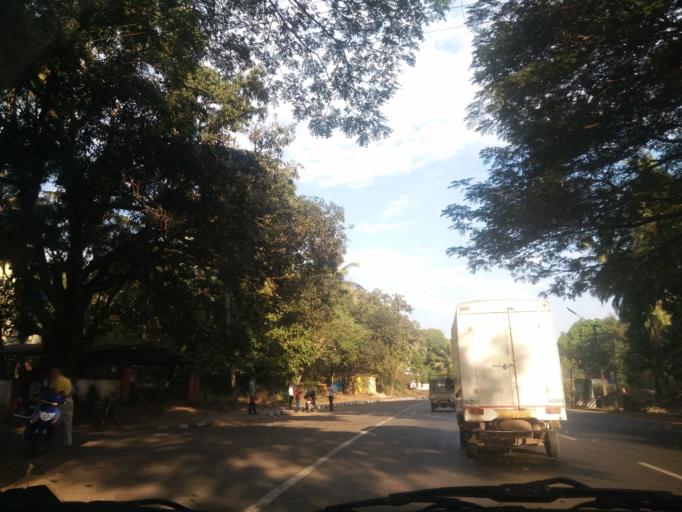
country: IN
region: Goa
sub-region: South Goa
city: Chinchinim
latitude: 15.2439
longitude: 73.9728
